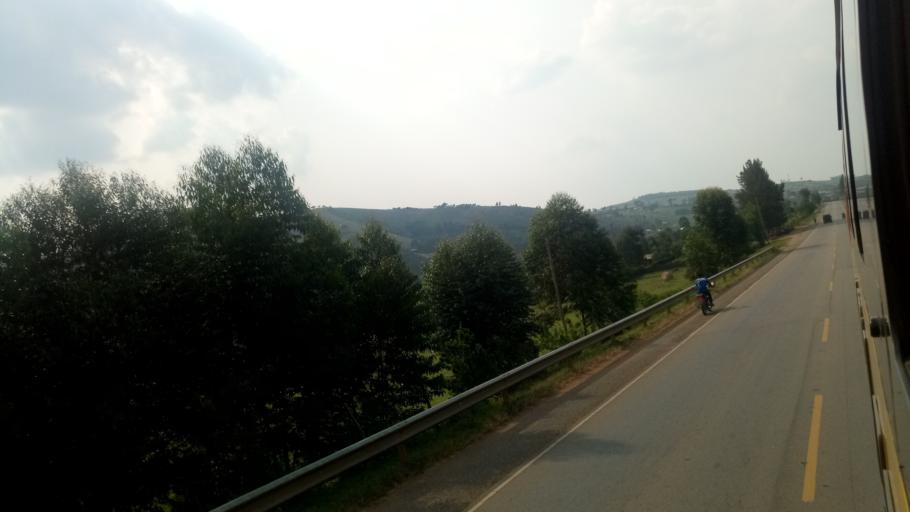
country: UG
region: Western Region
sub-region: Mbarara District
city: Mbarara
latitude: -0.5424
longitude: 30.7140
